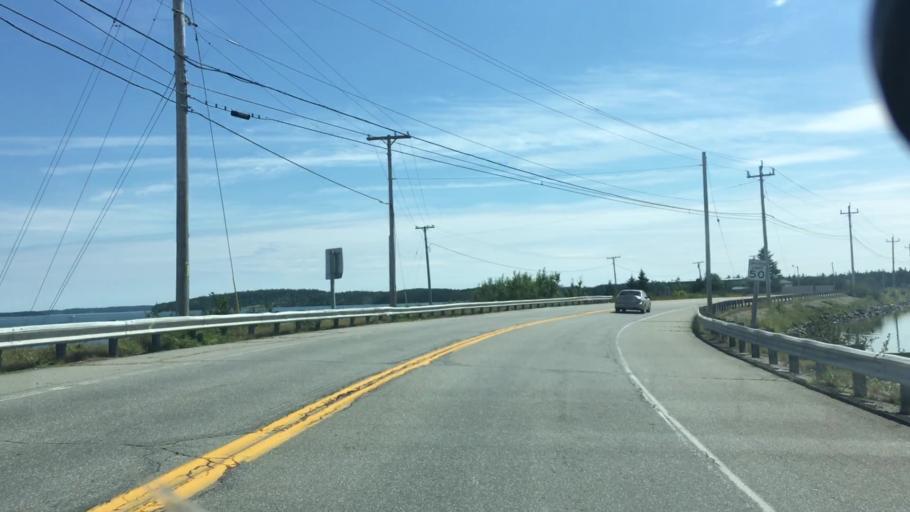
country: US
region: Maine
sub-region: Washington County
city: Eastport
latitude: 44.9539
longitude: -67.0397
